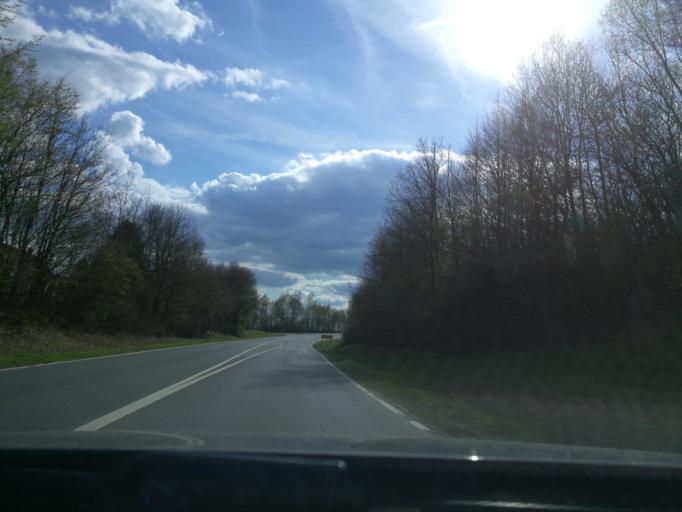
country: DE
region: Bavaria
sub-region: Upper Franconia
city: Weilersbach
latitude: 49.8088
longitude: 11.1127
